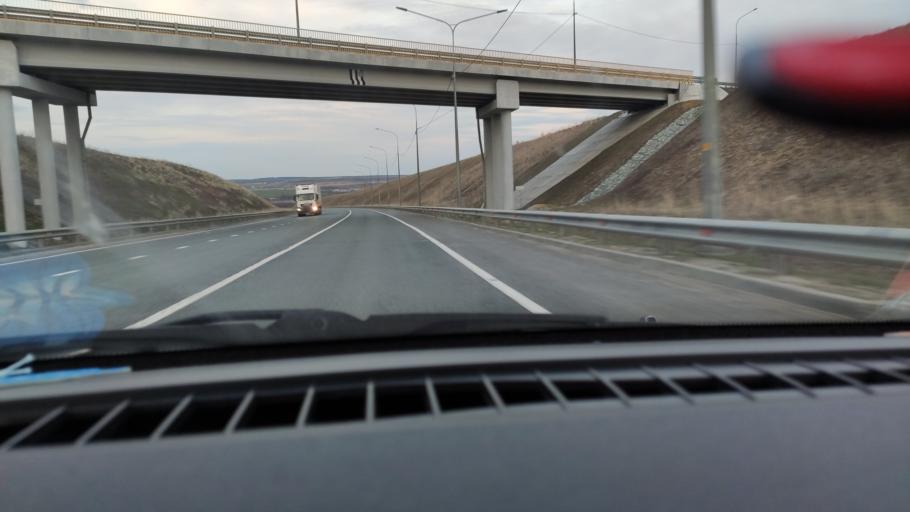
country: RU
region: Saratov
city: Yelshanka
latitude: 51.8209
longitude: 46.3706
